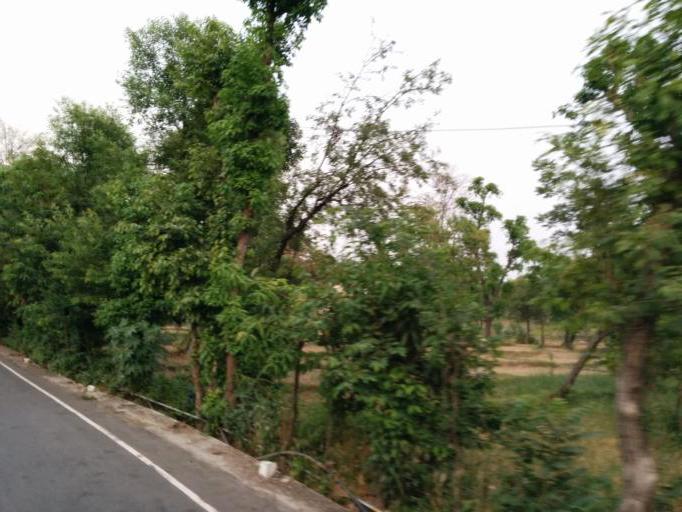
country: IN
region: Himachal Pradesh
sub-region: Kangra
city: Kangra
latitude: 32.1564
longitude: 76.2726
